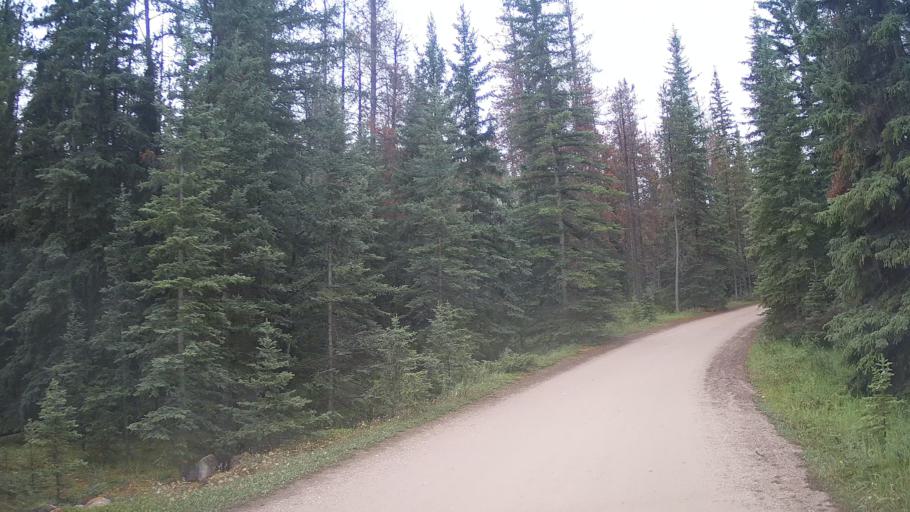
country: CA
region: Alberta
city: Jasper Park Lodge
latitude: 52.8615
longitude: -118.0708
